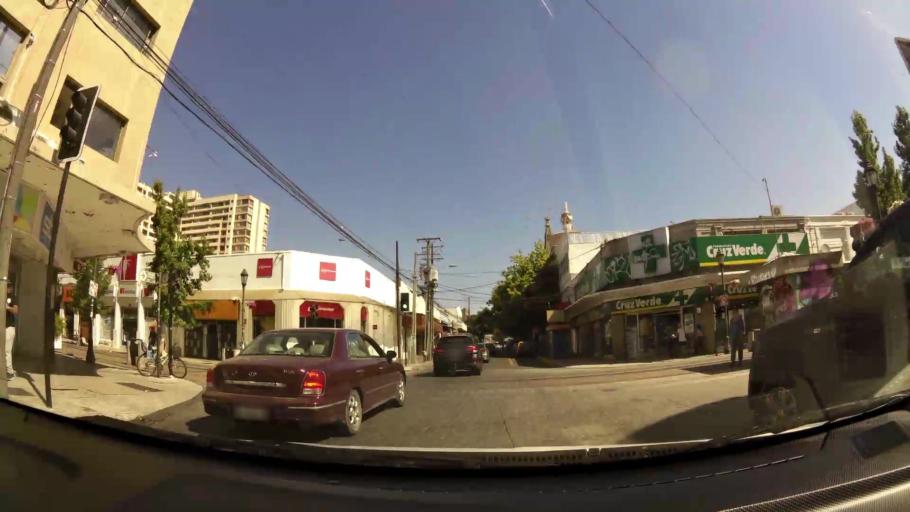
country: CL
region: Maule
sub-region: Provincia de Talca
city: Talca
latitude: -35.4275
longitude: -71.6599
